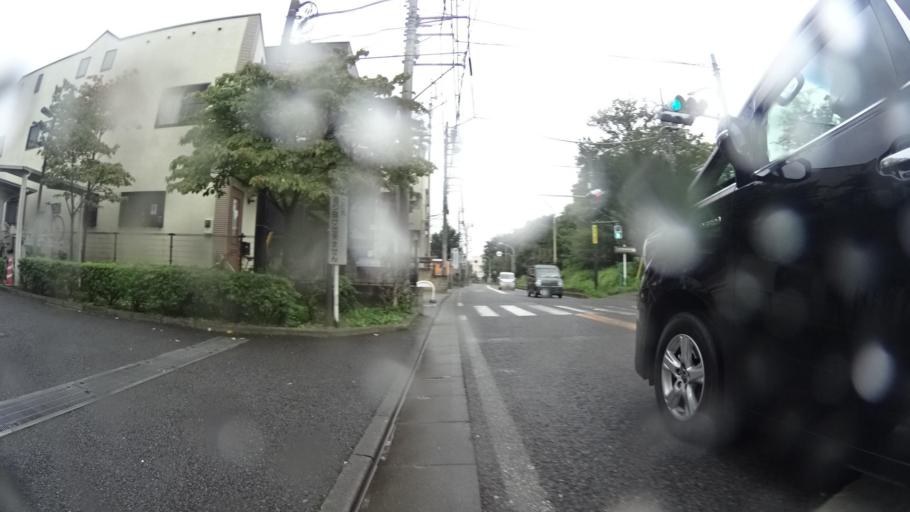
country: JP
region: Tokyo
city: Kokubunji
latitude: 35.7175
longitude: 139.4749
